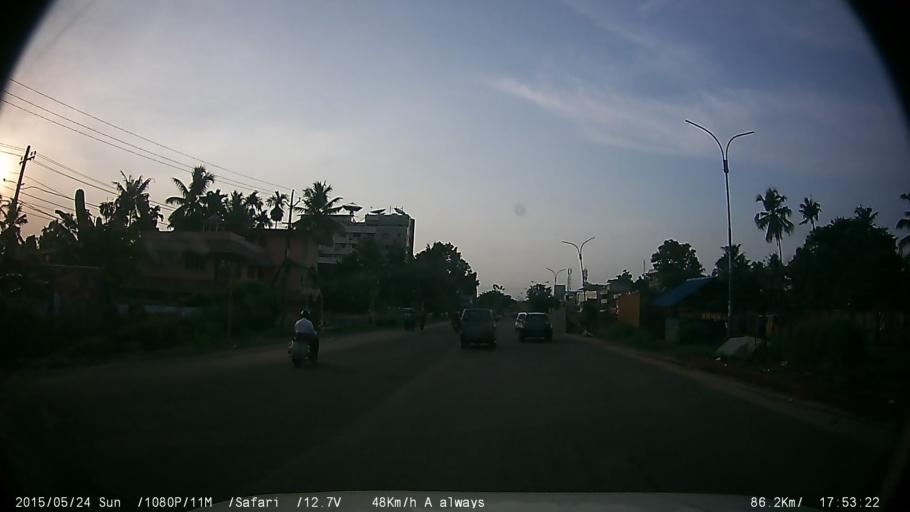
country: IN
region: Kerala
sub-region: Ernakulam
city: Elur
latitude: 10.0071
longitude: 76.3126
